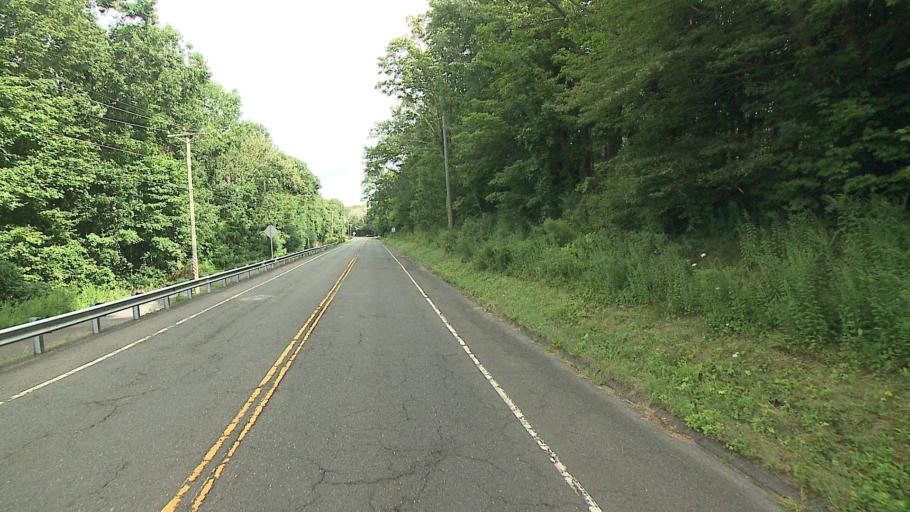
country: US
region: Connecticut
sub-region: New Haven County
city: Middlebury
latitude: 41.5236
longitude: -73.1388
